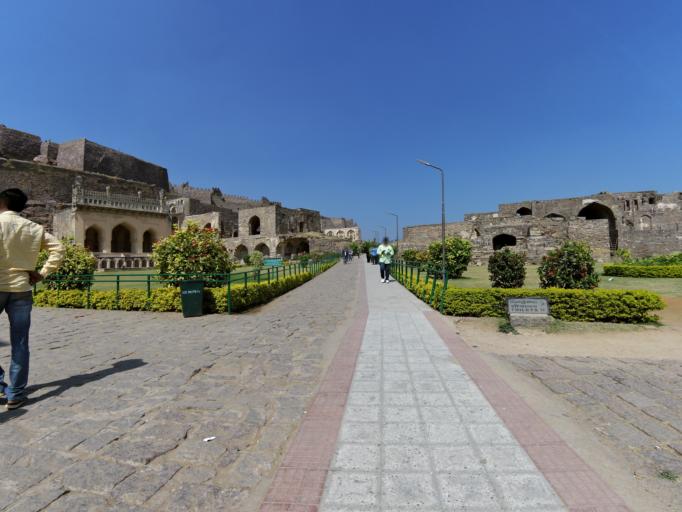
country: IN
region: Telangana
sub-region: Hyderabad
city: Hyderabad
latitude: 17.3830
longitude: 78.4019
